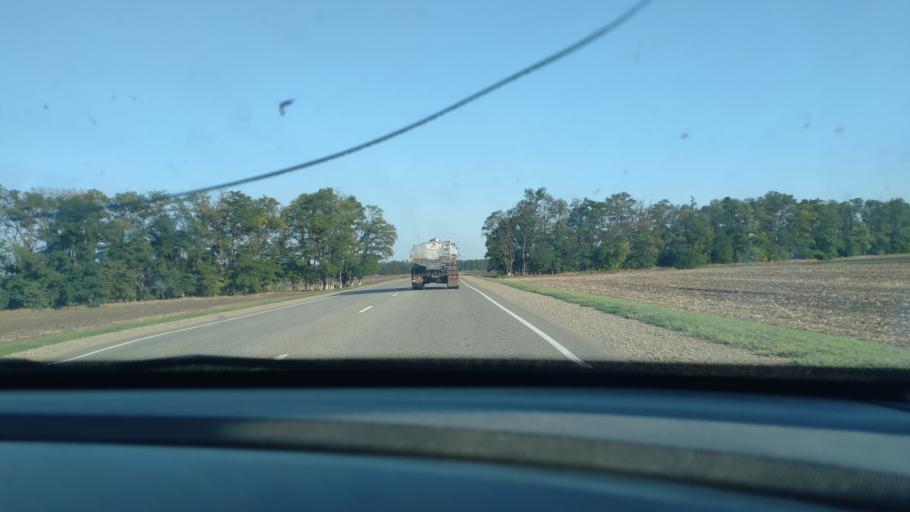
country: RU
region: Krasnodarskiy
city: Starominskaya
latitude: 46.4998
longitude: 39.0461
